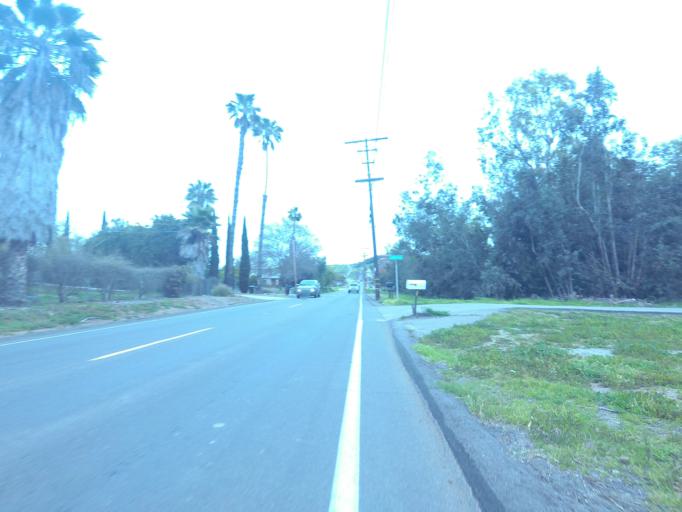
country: US
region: California
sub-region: San Diego County
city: Vista
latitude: 33.2377
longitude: -117.2299
